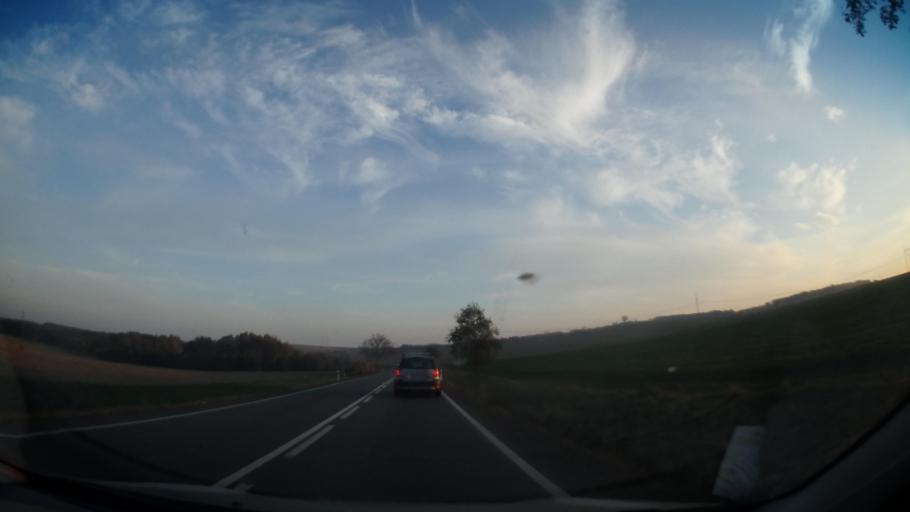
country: CZ
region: Central Bohemia
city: Trhovy Stepanov
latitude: 49.6697
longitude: 14.9735
